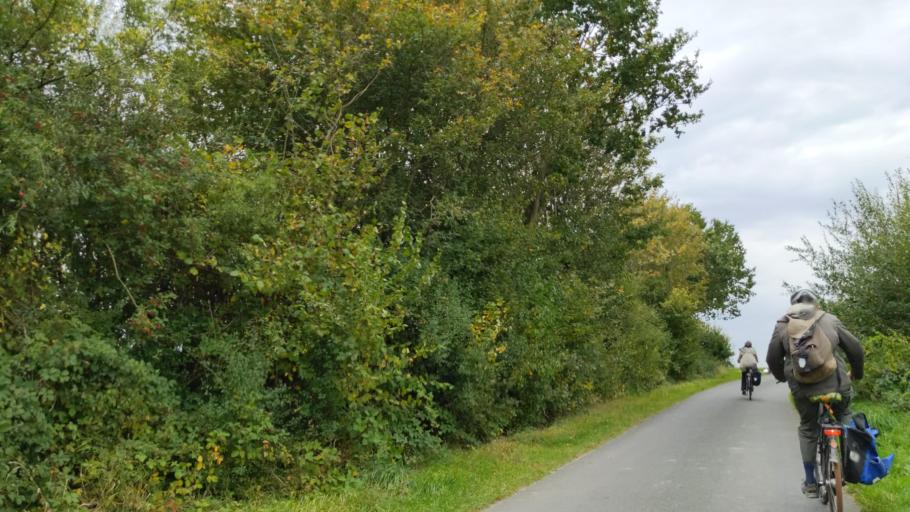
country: DE
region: Schleswig-Holstein
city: Bak
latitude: 53.7306
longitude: 10.7796
